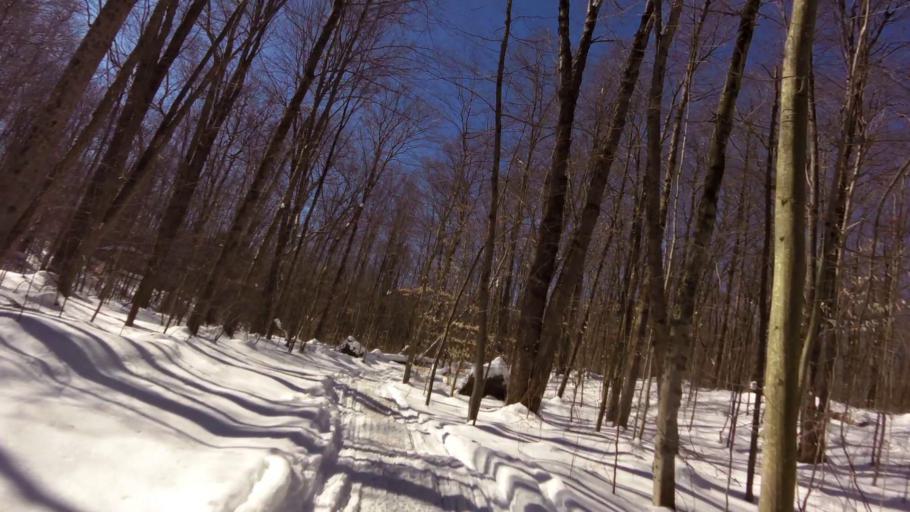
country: US
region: New York
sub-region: Allegany County
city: Cuba
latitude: 42.3244
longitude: -78.2755
